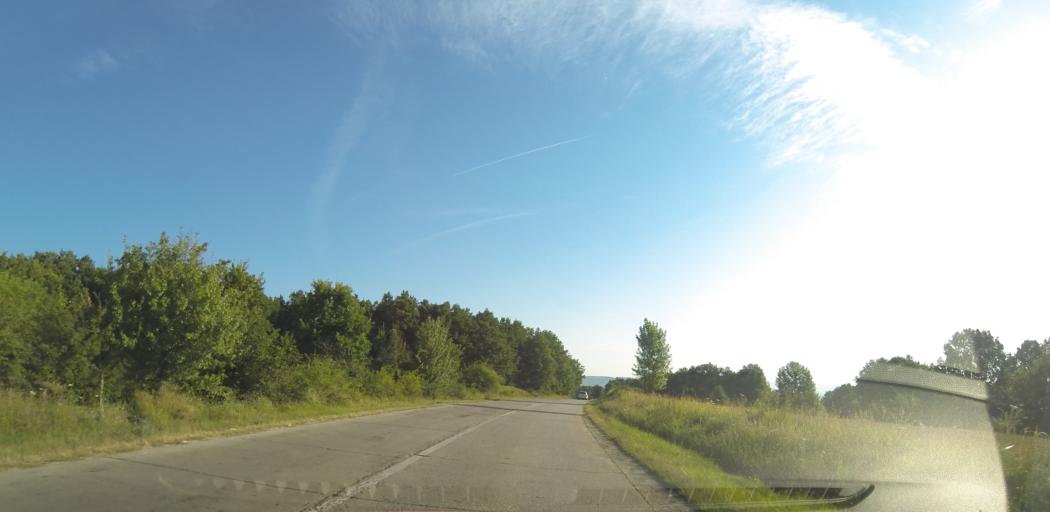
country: RO
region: Valcea
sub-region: Comuna Balcesti
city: Balcesti
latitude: 44.6049
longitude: 23.9294
